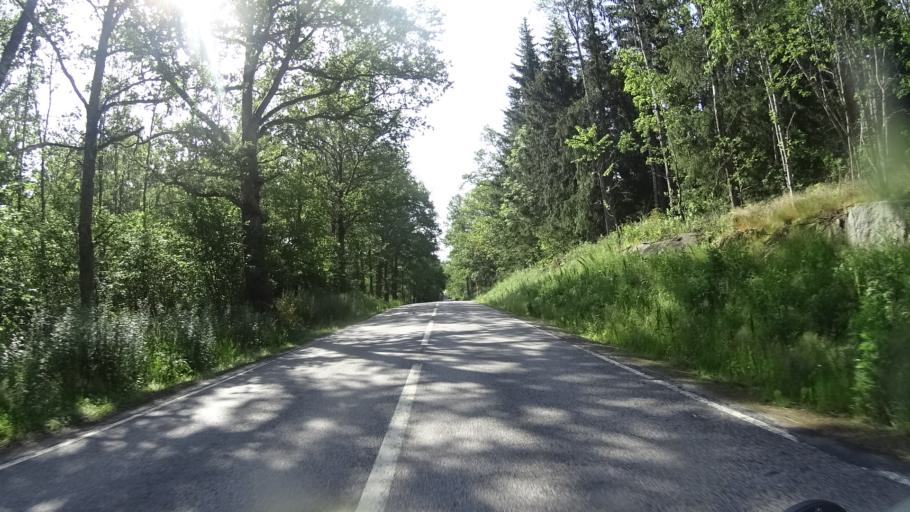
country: SE
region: Kalmar
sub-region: Vasterviks Kommun
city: Overum
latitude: 58.0791
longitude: 16.1822
